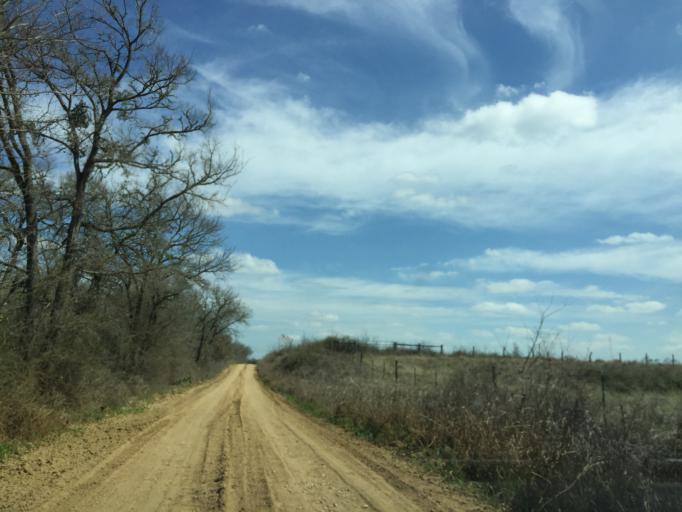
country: US
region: Texas
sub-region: Milam County
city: Thorndale
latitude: 30.5593
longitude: -97.1896
